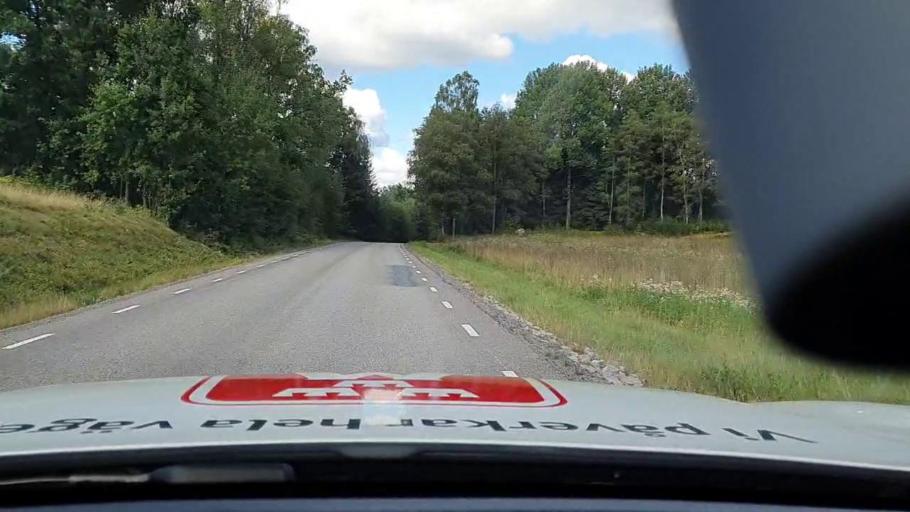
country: SE
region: Vaestra Goetaland
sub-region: Marks Kommun
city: Fritsla
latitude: 57.3986
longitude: 12.8508
